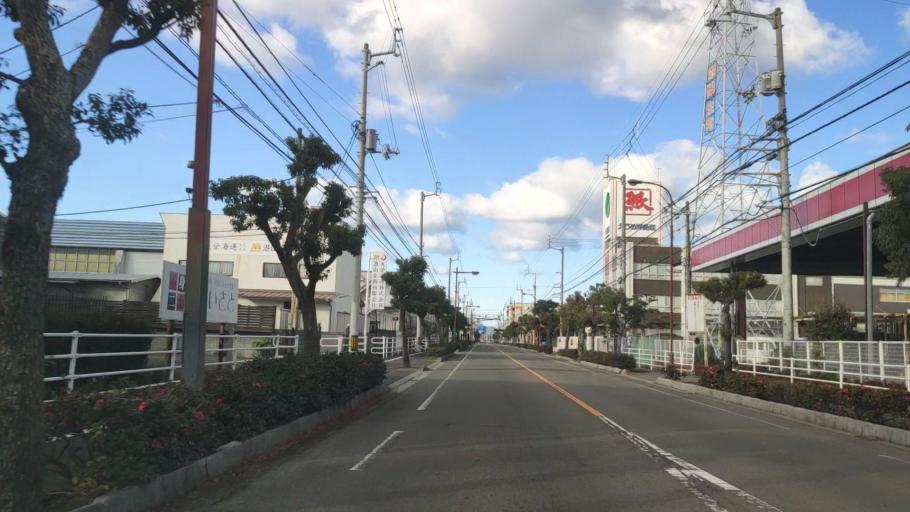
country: JP
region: Ehime
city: Masaki-cho
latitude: 33.8282
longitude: 132.7186
